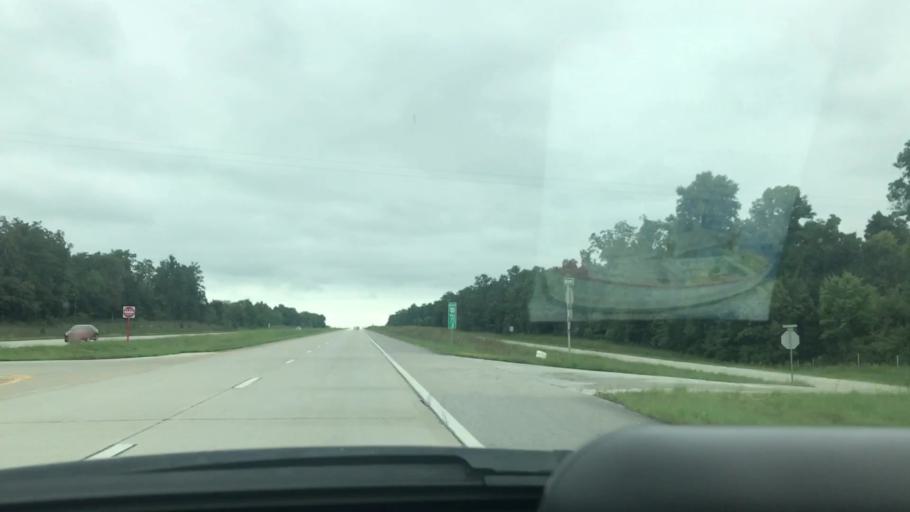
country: US
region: Missouri
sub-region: Greene County
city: Fair Grove
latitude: 37.4741
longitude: -93.1394
